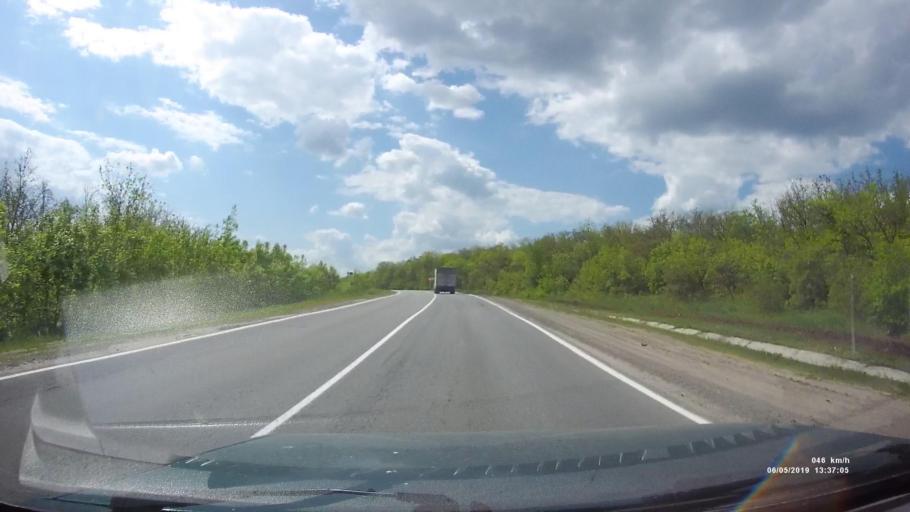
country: RU
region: Rostov
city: Ust'-Donetskiy
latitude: 47.6896
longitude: 40.7220
